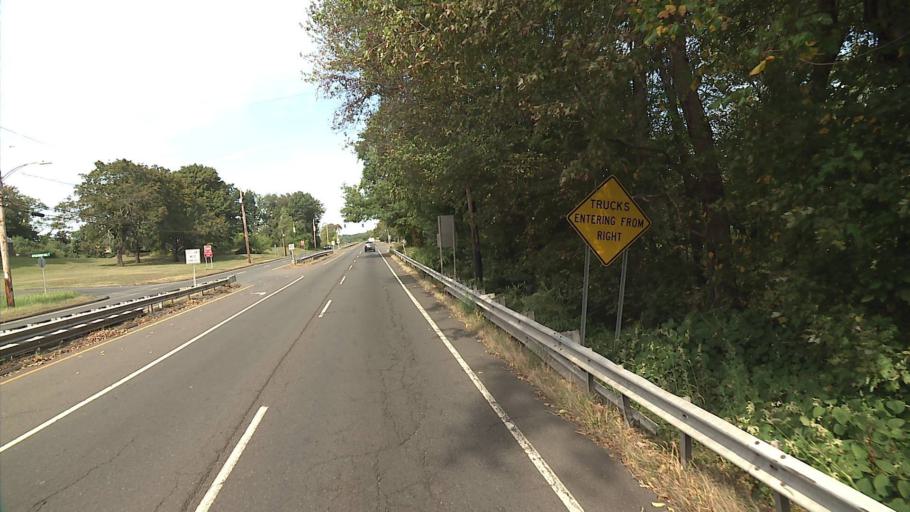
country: US
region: Connecticut
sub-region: New Haven County
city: Orange
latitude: 41.3084
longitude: -73.0372
